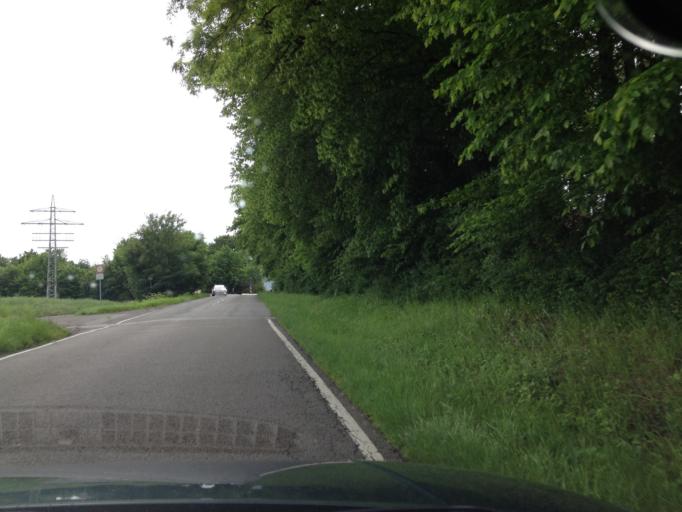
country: DE
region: Rheinland-Pfalz
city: Zweibrucken
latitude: 49.2440
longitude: 7.3872
